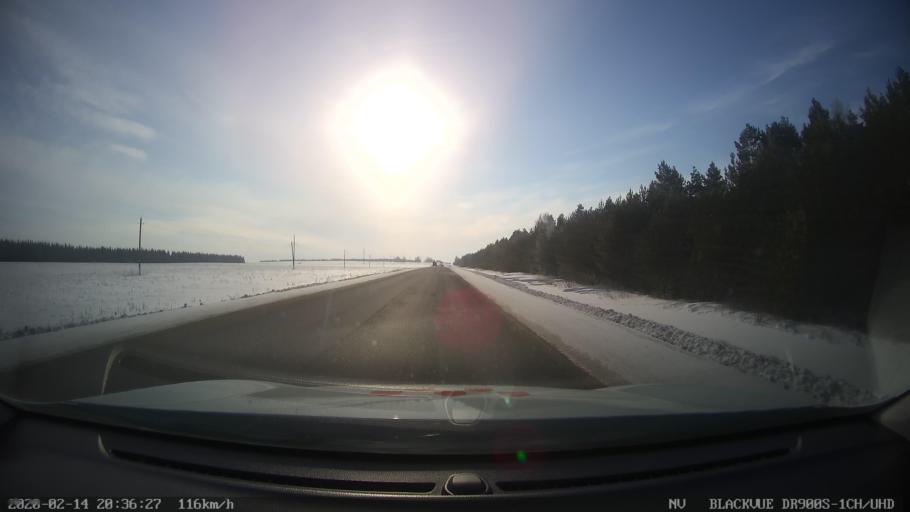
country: RU
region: Tatarstan
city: Kuybyshevskiy Zaton
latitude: 55.3671
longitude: 49.0000
